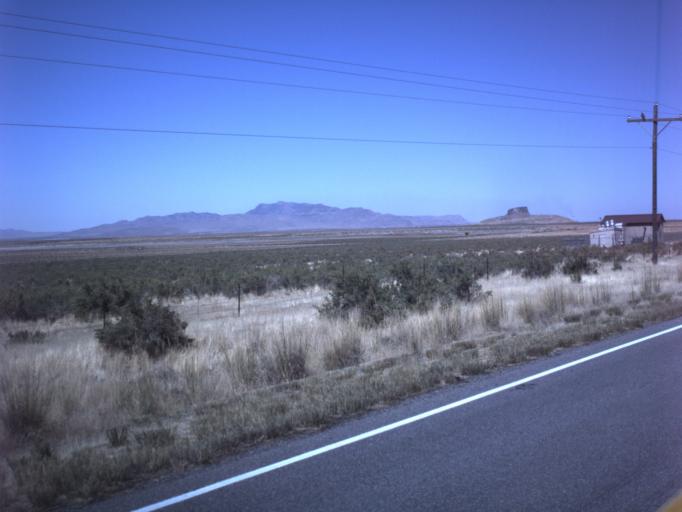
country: US
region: Utah
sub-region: Tooele County
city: Grantsville
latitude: 40.6746
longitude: -112.6729
